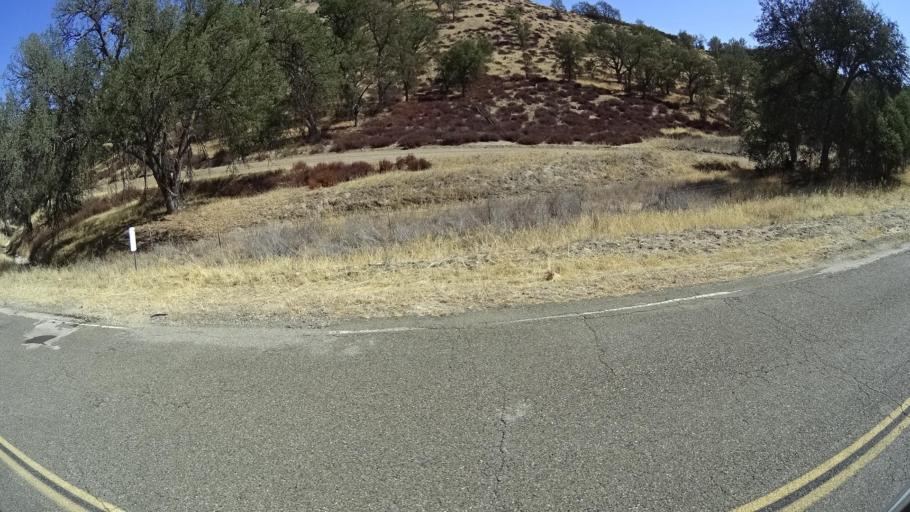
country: US
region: California
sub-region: San Luis Obispo County
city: Lake Nacimiento
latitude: 35.9108
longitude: -121.0885
